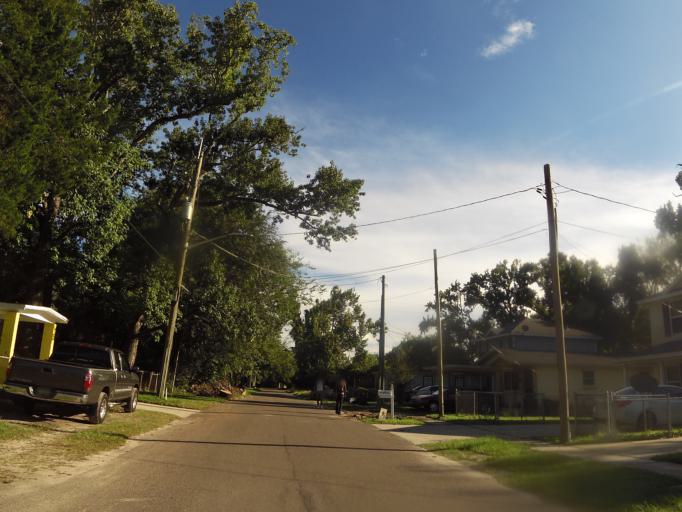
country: US
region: Florida
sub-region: Duval County
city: Jacksonville
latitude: 30.3497
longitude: -81.6898
